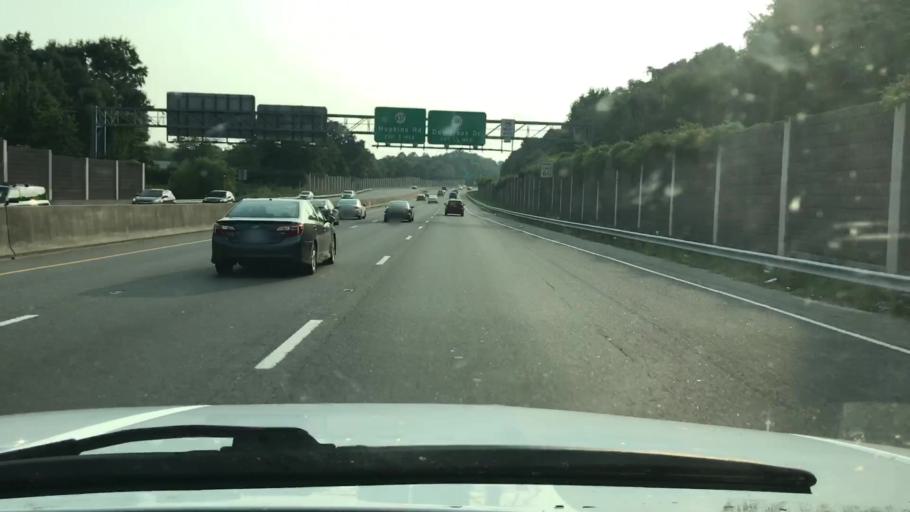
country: US
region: Virginia
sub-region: Chesterfield County
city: Bensley
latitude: 37.4408
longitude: -77.4565
